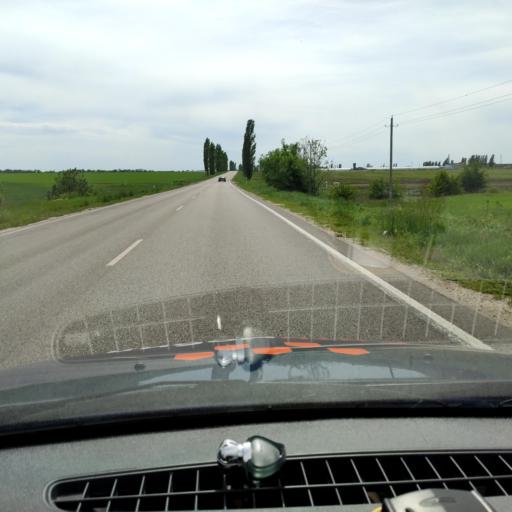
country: RU
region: Voronezj
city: Novaya Usman'
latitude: 51.5526
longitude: 39.3715
